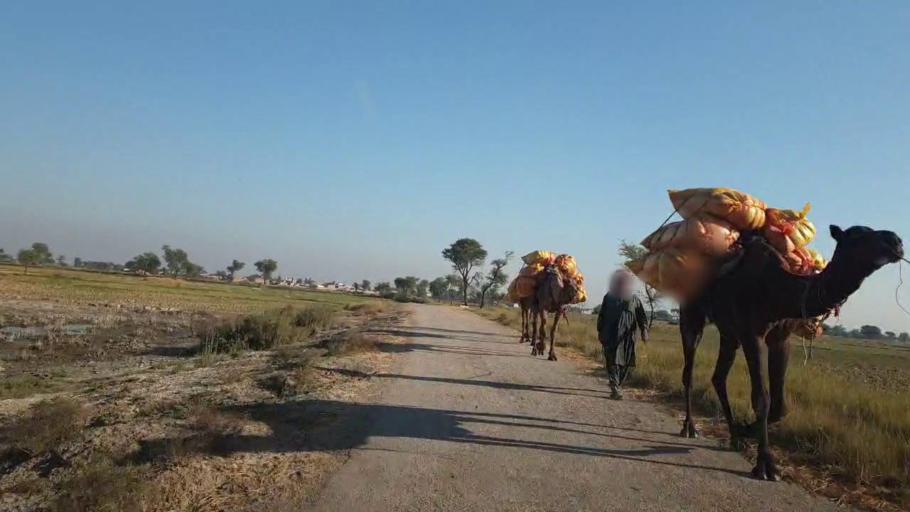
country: PK
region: Sindh
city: Phulji
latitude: 26.9883
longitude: 67.6893
